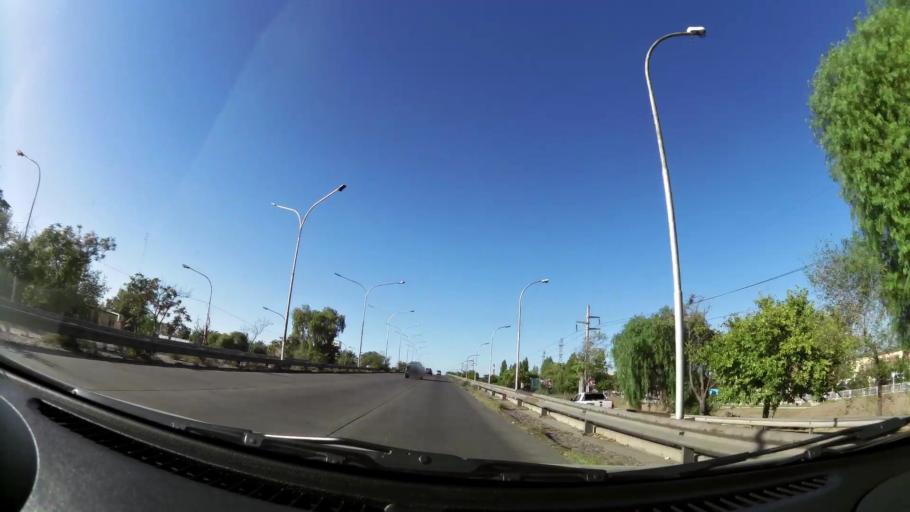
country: AR
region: Mendoza
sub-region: Departamento de Godoy Cruz
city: Godoy Cruz
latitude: -32.9172
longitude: -68.8375
